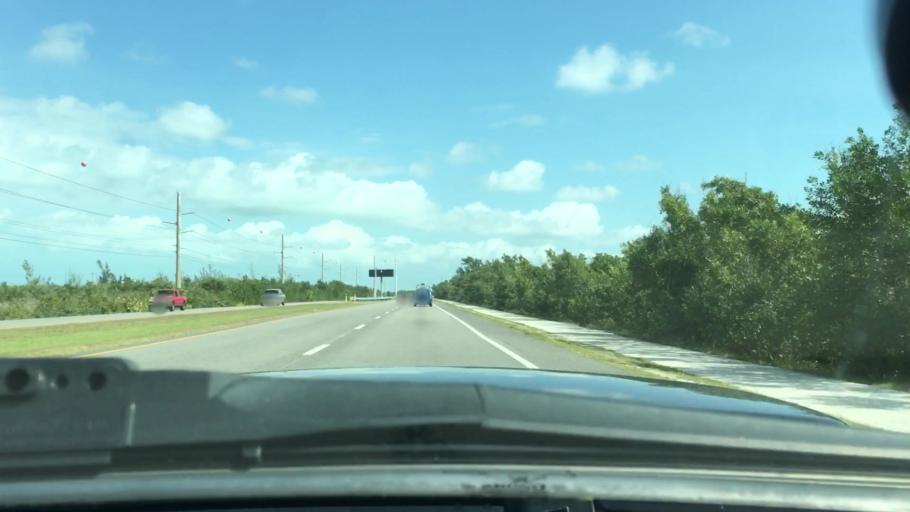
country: US
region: Florida
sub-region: Monroe County
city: Big Coppitt Key
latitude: 24.5841
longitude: -81.7000
